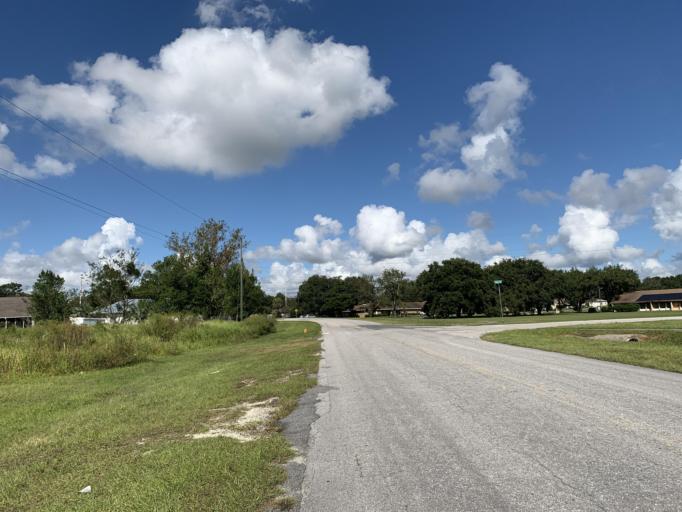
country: US
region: Florida
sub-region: Marion County
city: Silver Springs Shores
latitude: 29.1595
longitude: -82.0506
